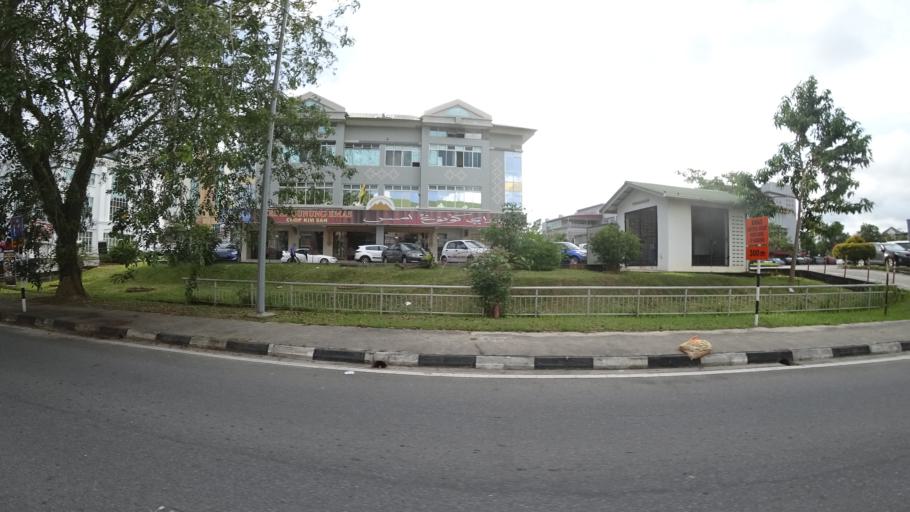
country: BN
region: Brunei and Muara
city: Bandar Seri Begawan
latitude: 4.9036
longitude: 114.9275
